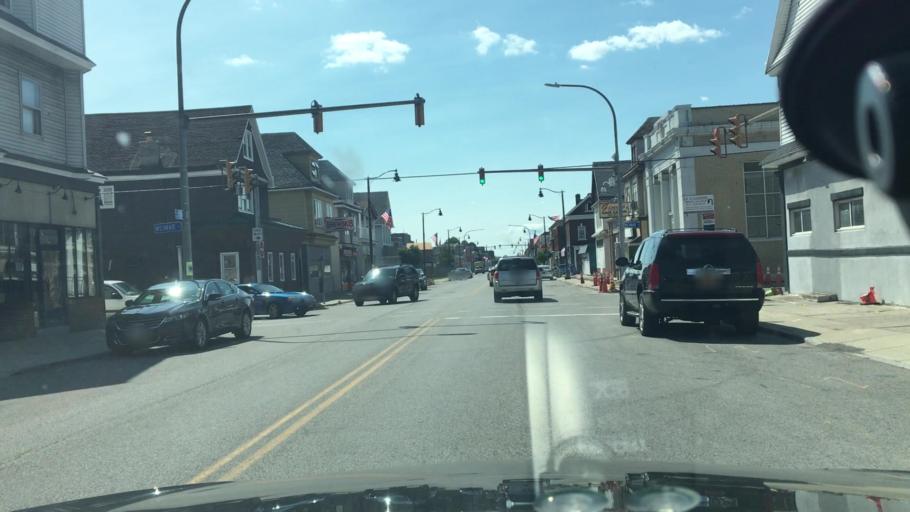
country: US
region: New York
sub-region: Erie County
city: West Seneca
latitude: 42.8719
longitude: -78.8073
